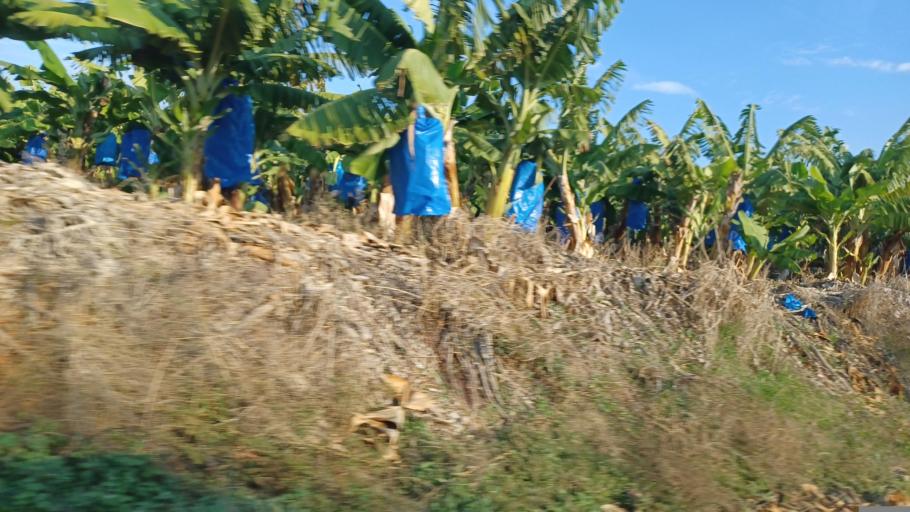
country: CY
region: Pafos
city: Pegeia
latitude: 34.8952
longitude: 32.3375
